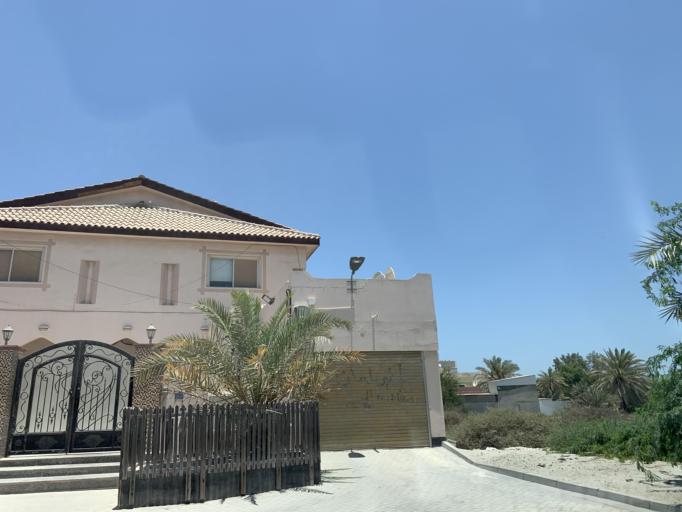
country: BH
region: Manama
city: Jidd Hafs
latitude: 26.2281
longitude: 50.4819
